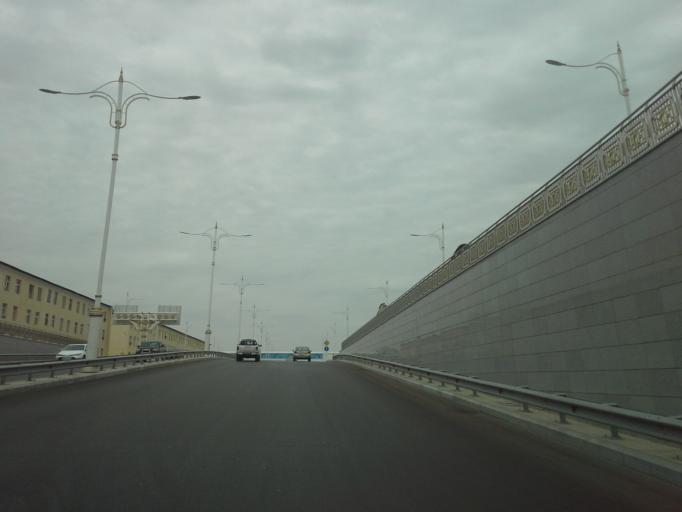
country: TM
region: Ahal
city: Ashgabat
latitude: 37.9448
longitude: 58.4049
